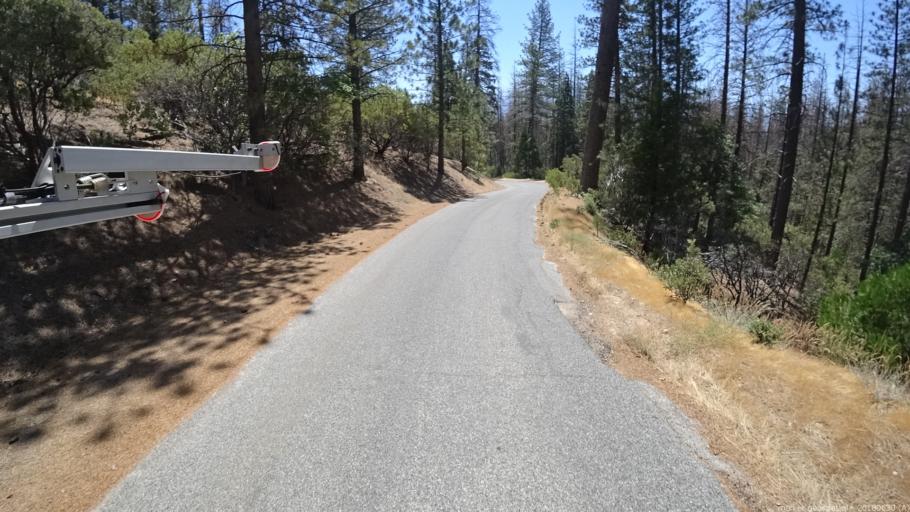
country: US
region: California
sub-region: Madera County
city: Oakhurst
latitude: 37.3553
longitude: -119.3440
